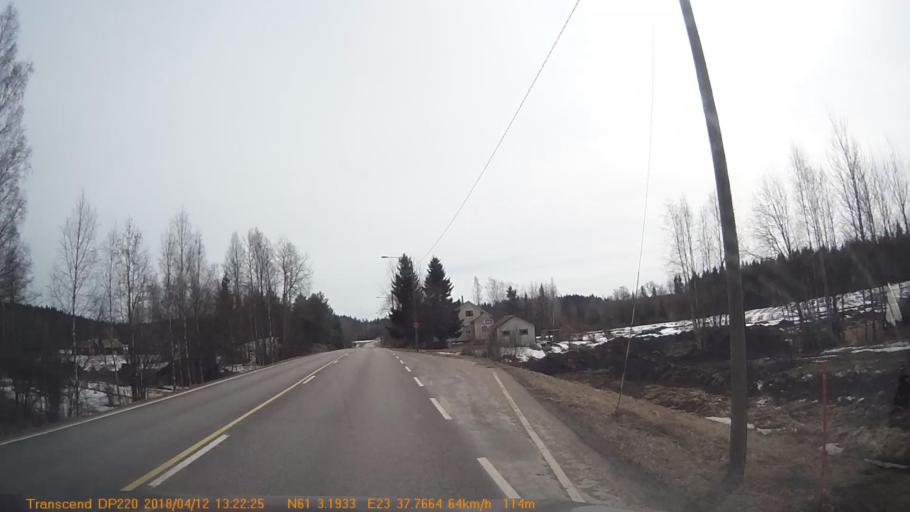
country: FI
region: Pirkanmaa
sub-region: Etelae-Pirkanmaa
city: Urjala
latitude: 61.0525
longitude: 23.6303
